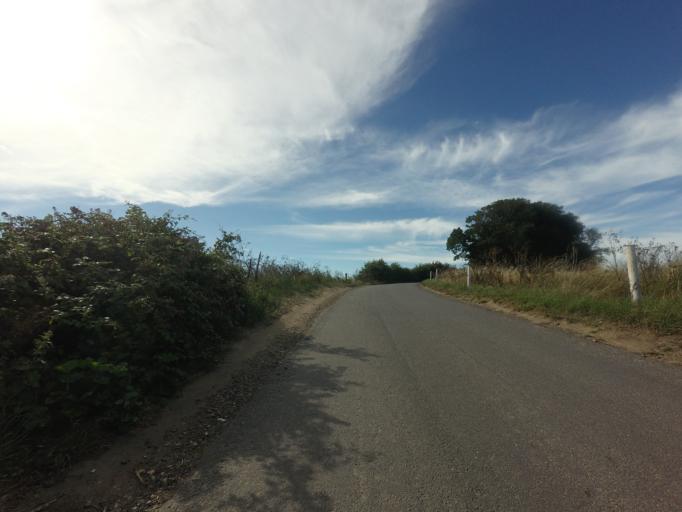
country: GB
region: England
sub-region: Kent
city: Herne Bay
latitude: 51.3701
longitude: 1.1858
